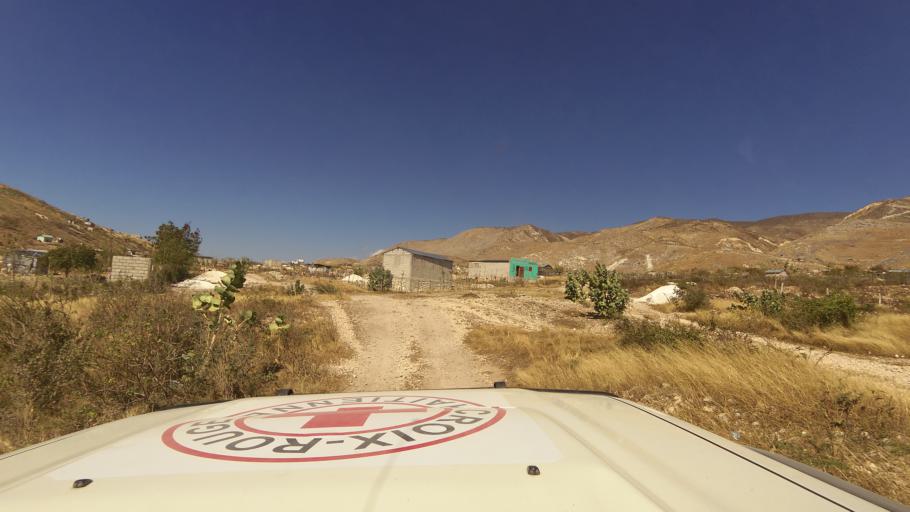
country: HT
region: Ouest
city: Croix des Bouquets
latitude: 18.6729
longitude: -72.2864
